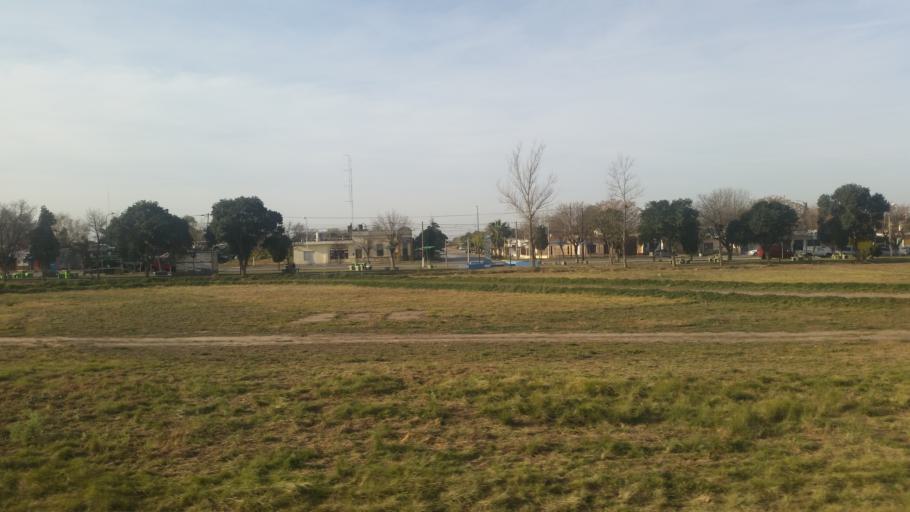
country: AR
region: Cordoba
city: Toledo
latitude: -31.5571
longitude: -64.0086
